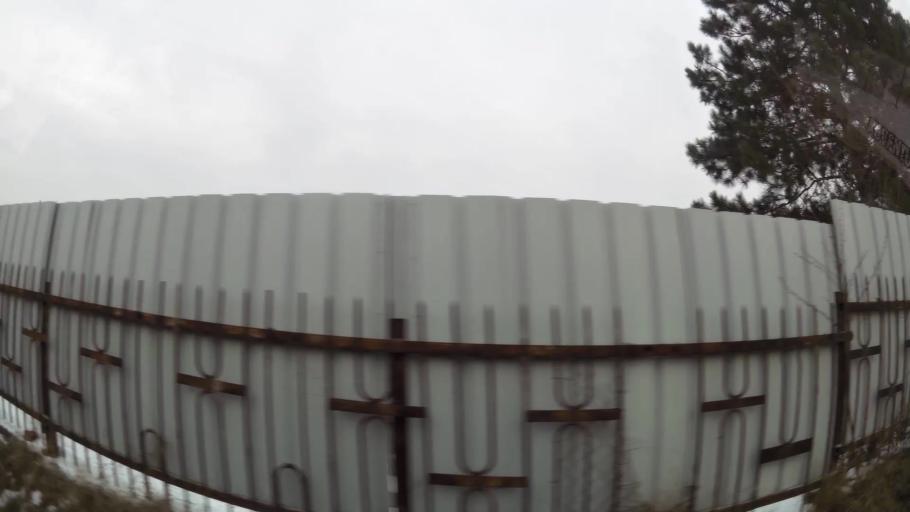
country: MK
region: Suto Orizari
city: Suto Orizare
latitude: 42.0427
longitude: 21.4303
